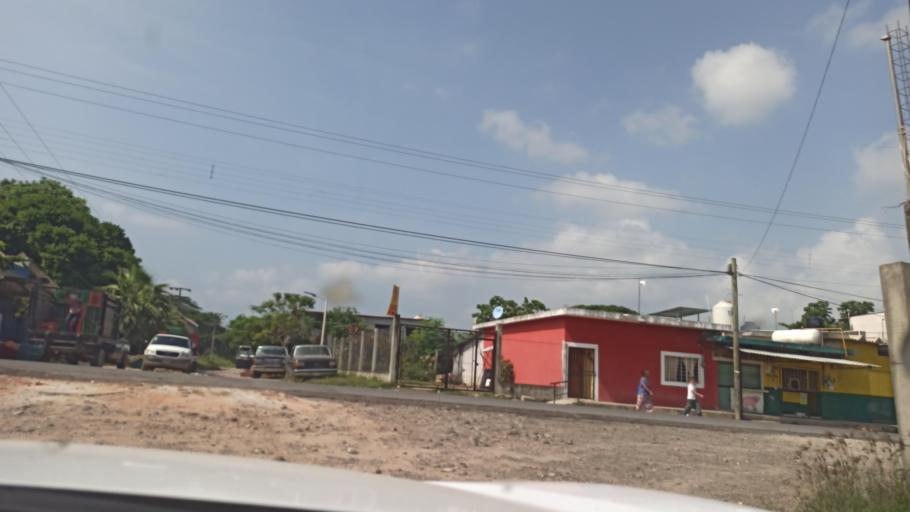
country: MX
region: Veracruz
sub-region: Martinez de la Torre
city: El Progreso
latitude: 20.1464
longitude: -97.0640
